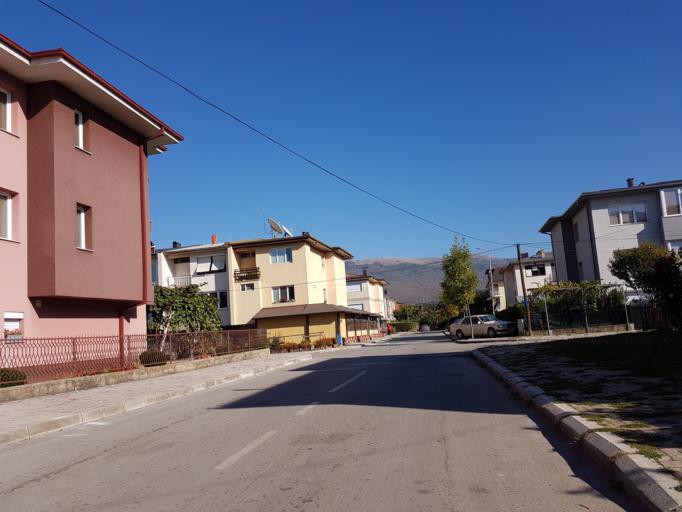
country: MK
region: Ohrid
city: Ohrid
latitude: 41.1232
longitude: 20.7808
